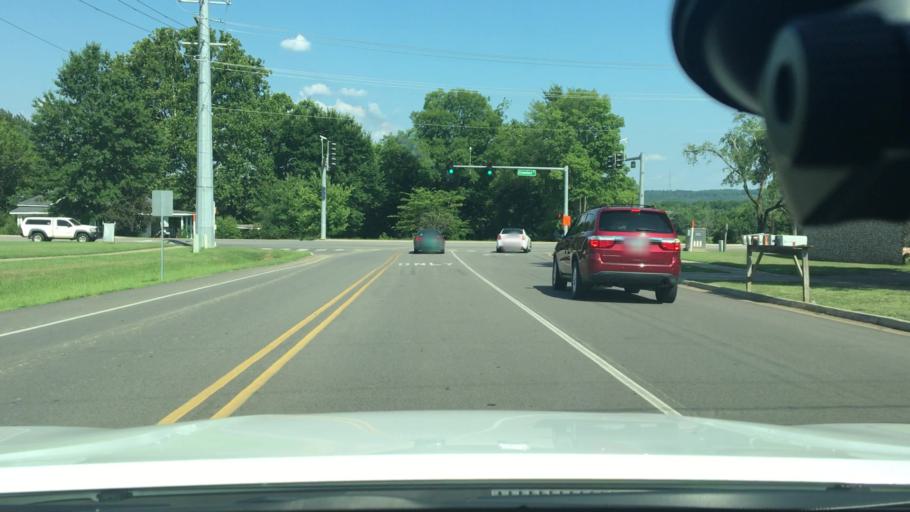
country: US
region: Arkansas
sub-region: Johnson County
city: Clarksville
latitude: 35.4614
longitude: -93.4817
